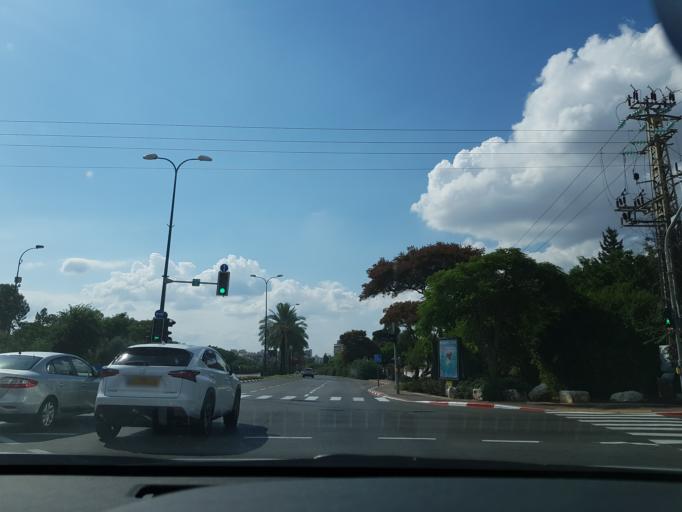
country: IL
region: Central District
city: Ness Ziona
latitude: 31.9368
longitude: 34.7998
